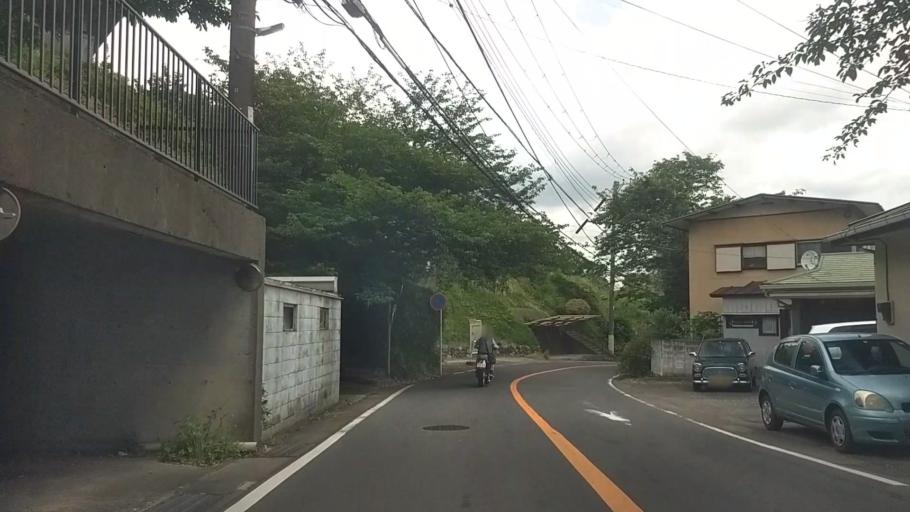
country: JP
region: Kanagawa
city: Kamakura
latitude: 35.3203
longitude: 139.5222
